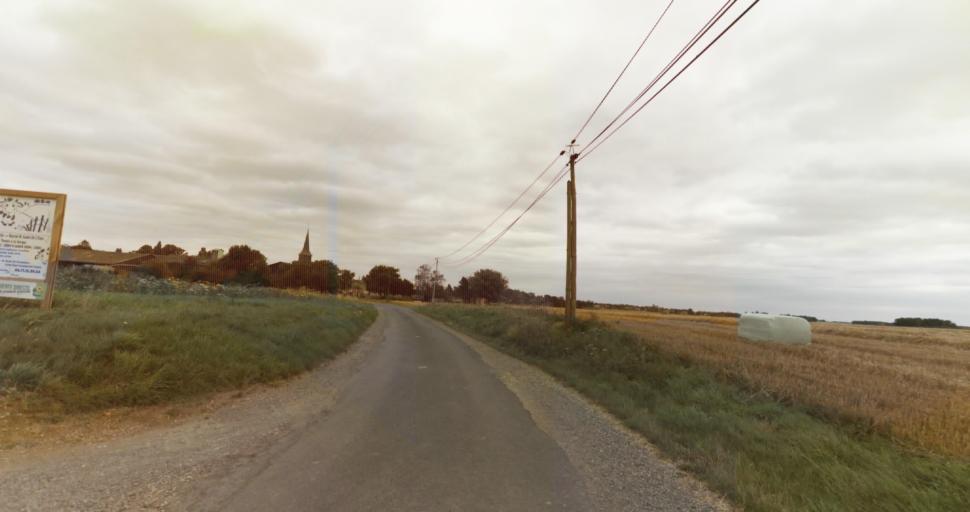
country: FR
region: Haute-Normandie
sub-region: Departement de l'Eure
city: Menilles
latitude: 48.9585
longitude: 1.2870
